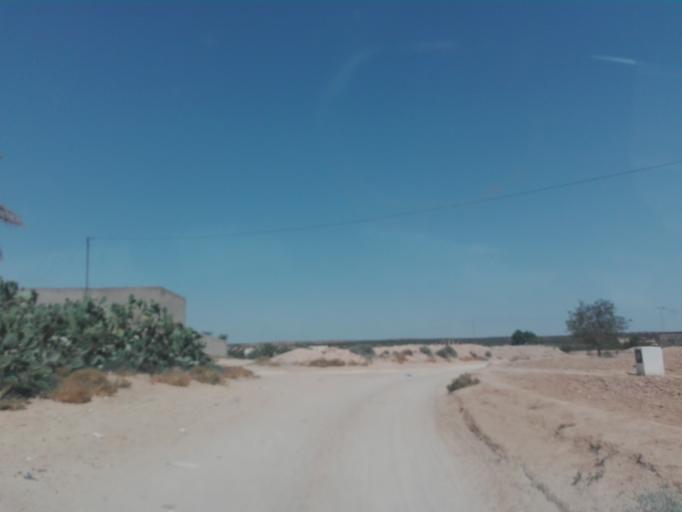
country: TN
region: Safaqis
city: Bi'r `Ali Bin Khalifah
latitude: 34.6476
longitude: 10.2574
